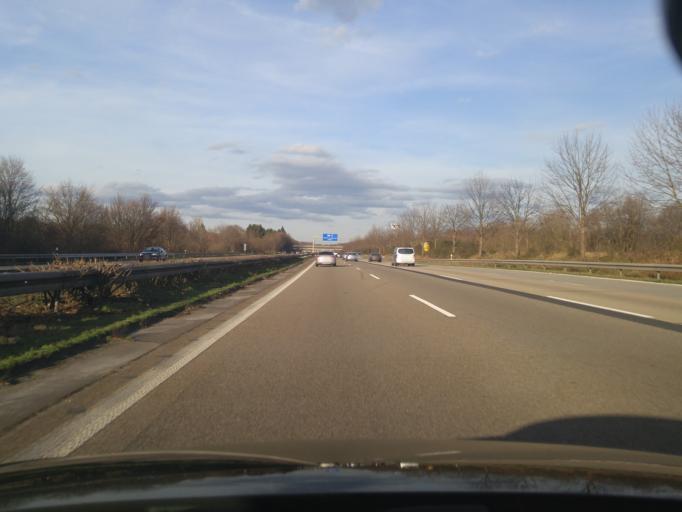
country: DE
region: North Rhine-Westphalia
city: Leichlingen
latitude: 51.0887
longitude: 6.9884
